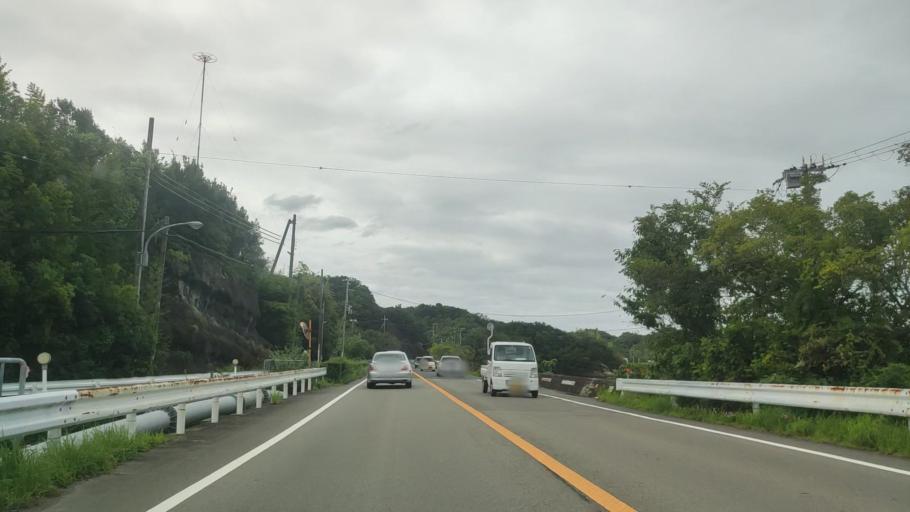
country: JP
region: Wakayama
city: Tanabe
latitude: 33.7043
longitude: 135.3967
